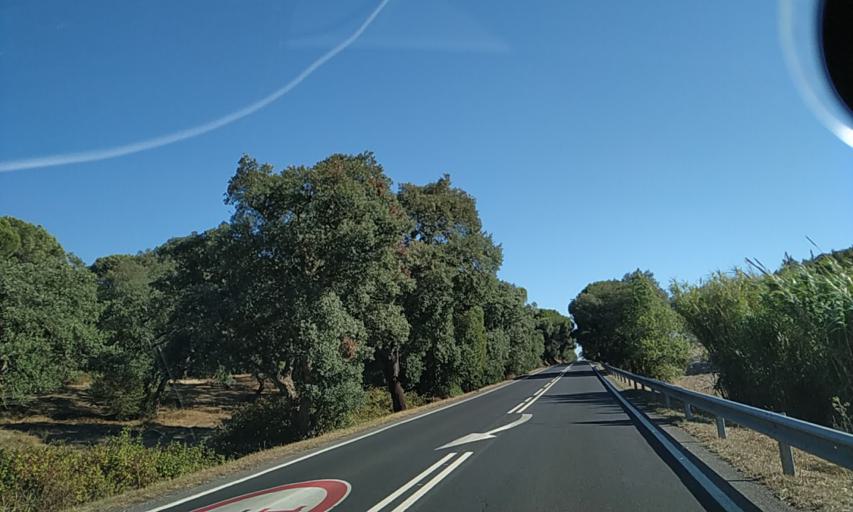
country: PT
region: Santarem
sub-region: Benavente
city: Samora Correia
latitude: 38.8963
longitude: -8.8814
